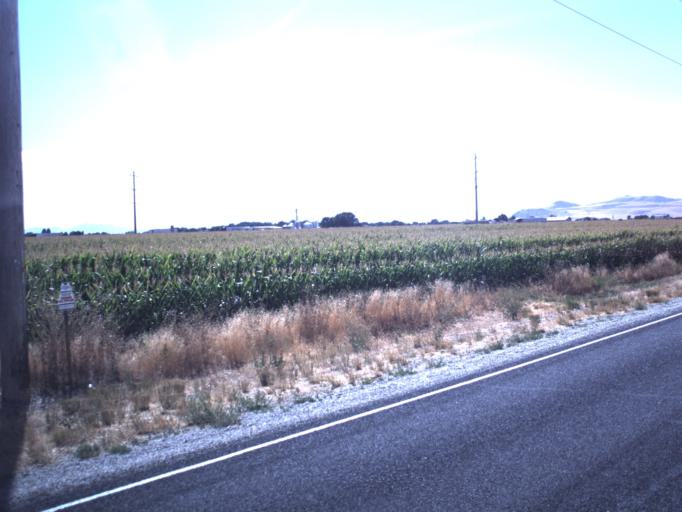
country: US
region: Utah
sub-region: Box Elder County
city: Honeyville
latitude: 41.6349
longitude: -112.0921
